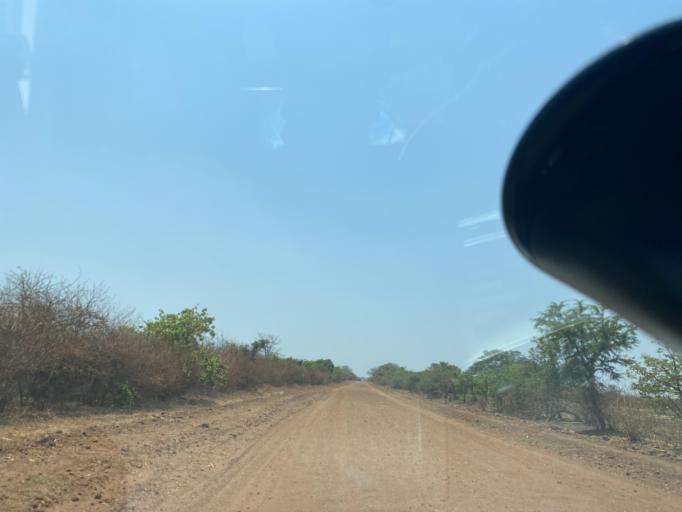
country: ZM
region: Lusaka
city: Lusaka
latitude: -15.4590
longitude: 27.9309
